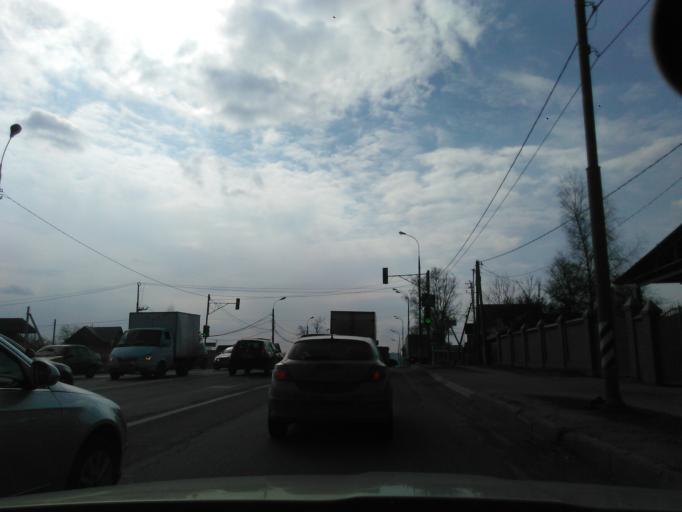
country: RU
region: Moscow
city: Severnyy
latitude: 55.9557
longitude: 37.5353
